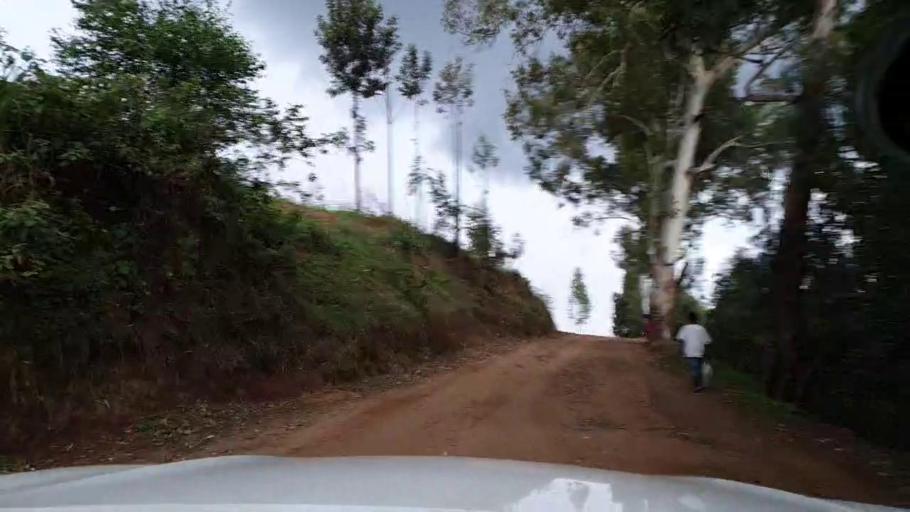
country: BI
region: Kayanza
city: Kayanza
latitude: -2.7890
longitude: 29.5268
